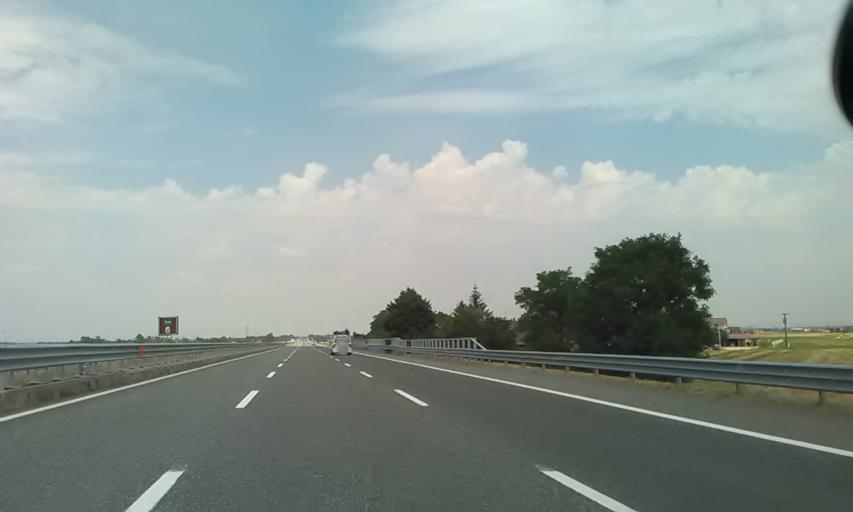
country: IT
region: Piedmont
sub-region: Provincia di Alessandria
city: Castelspina
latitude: 44.7880
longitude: 8.6165
